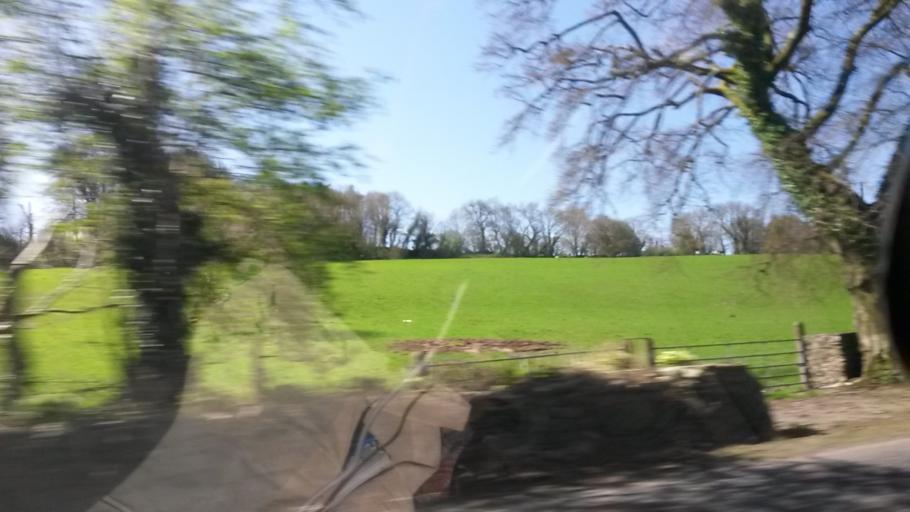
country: IE
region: Munster
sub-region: County Cork
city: Blarney
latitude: 51.8967
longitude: -8.5503
